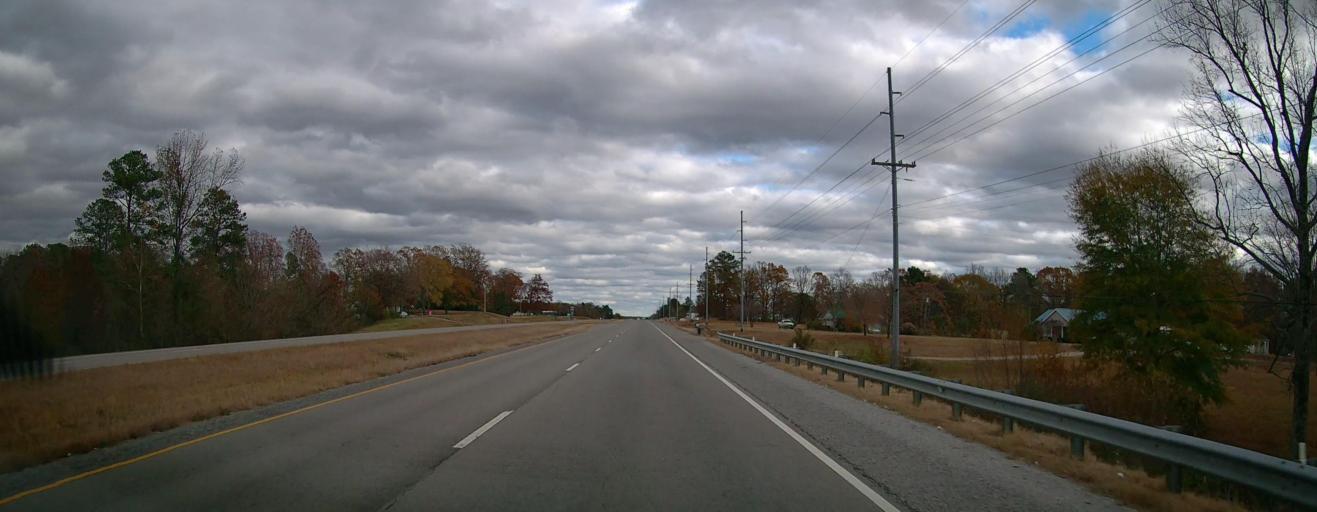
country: US
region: Alabama
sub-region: Lawrence County
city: Town Creek
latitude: 34.5687
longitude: -87.3780
